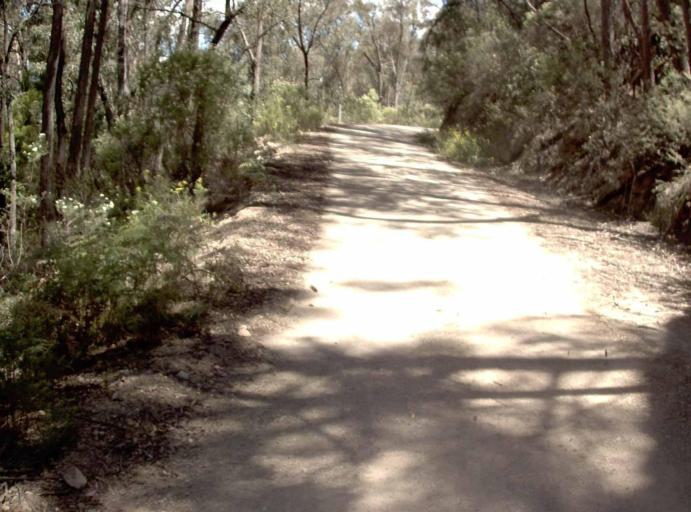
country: AU
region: New South Wales
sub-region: Snowy River
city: Jindabyne
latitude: -37.0822
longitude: 148.3347
